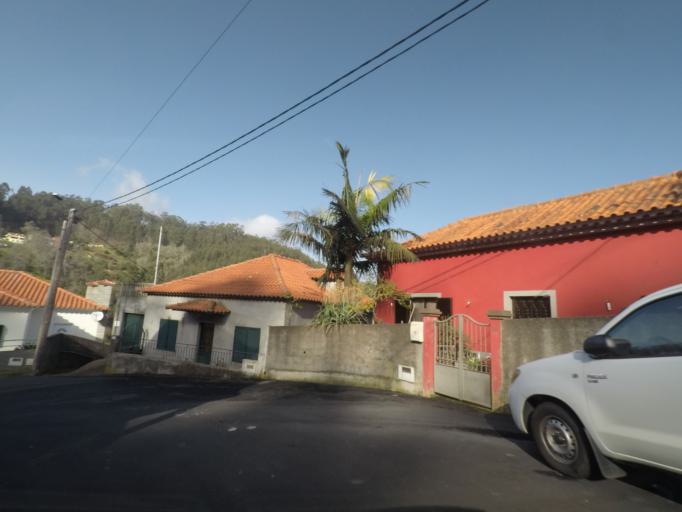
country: PT
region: Madeira
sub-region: Ribeira Brava
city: Campanario
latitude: 32.6778
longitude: -17.0077
